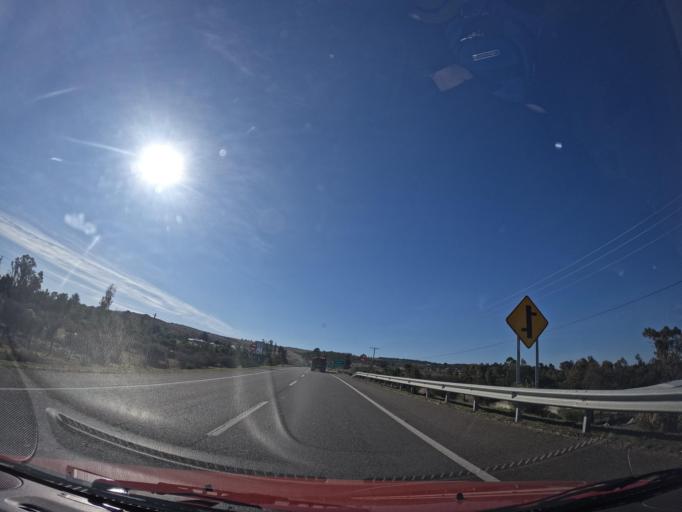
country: CL
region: Maule
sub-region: Provincia de Cauquenes
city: Cauquenes
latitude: -35.9456
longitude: -72.2010
